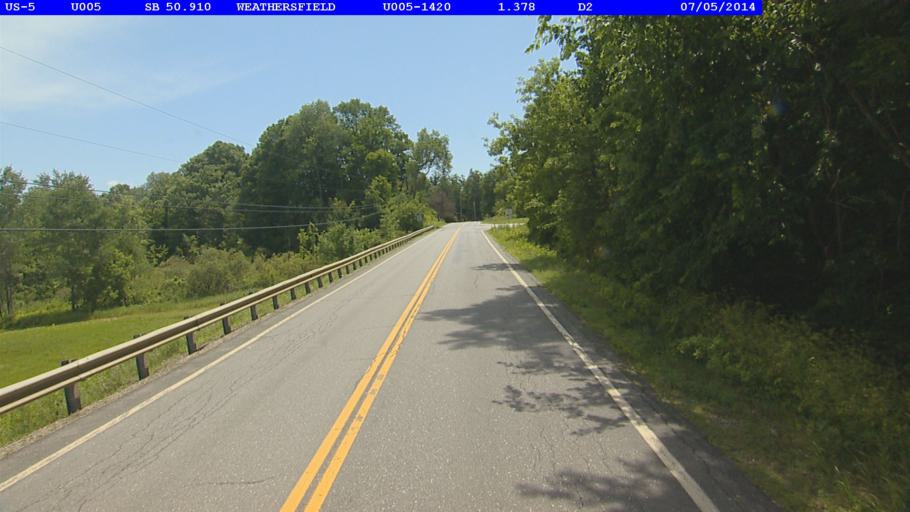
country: US
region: New Hampshire
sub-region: Sullivan County
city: Claremont
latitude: 43.3581
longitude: -72.4079
